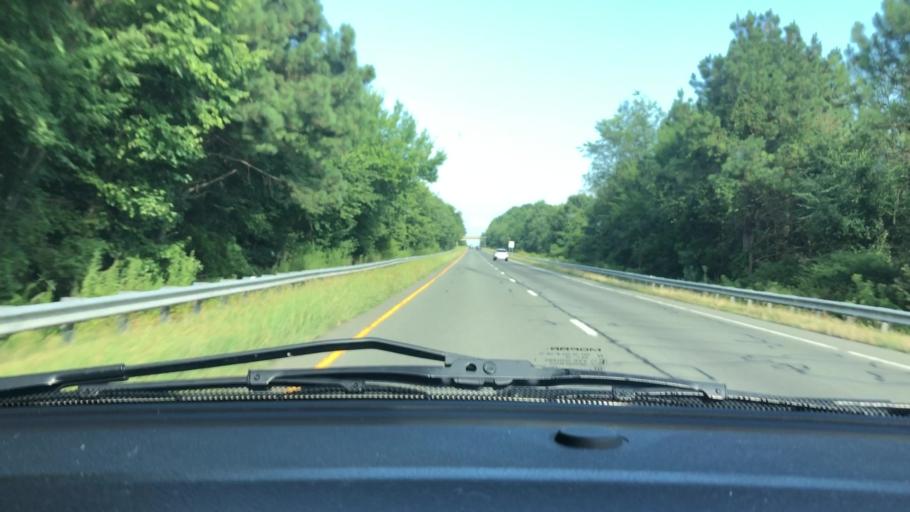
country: US
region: North Carolina
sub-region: Chatham County
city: Siler City
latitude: 35.7803
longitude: -79.5089
